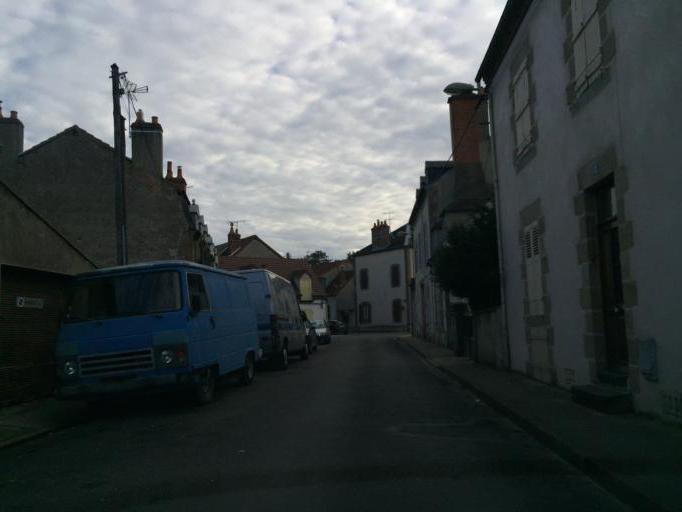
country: FR
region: Auvergne
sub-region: Departement de l'Allier
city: Moulins
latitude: 46.5691
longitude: 3.3387
